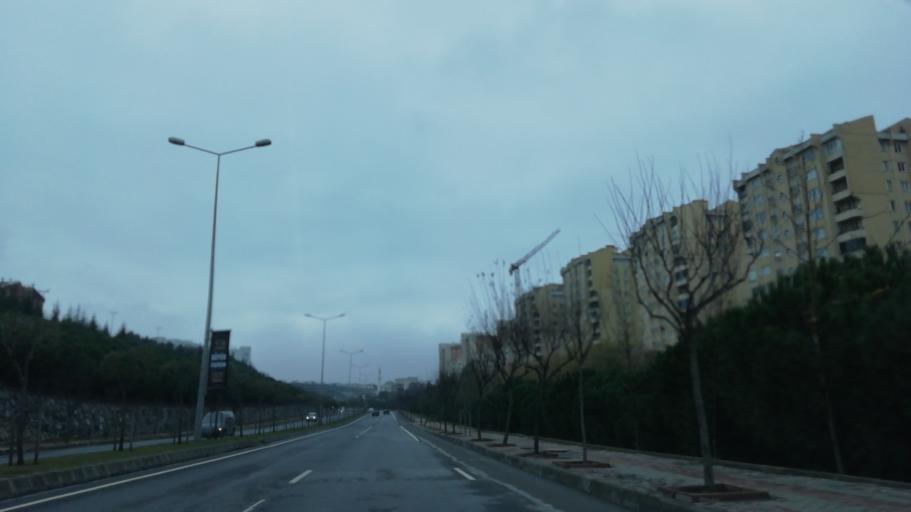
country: TR
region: Istanbul
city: Basaksehir
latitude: 41.0989
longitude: 28.8013
